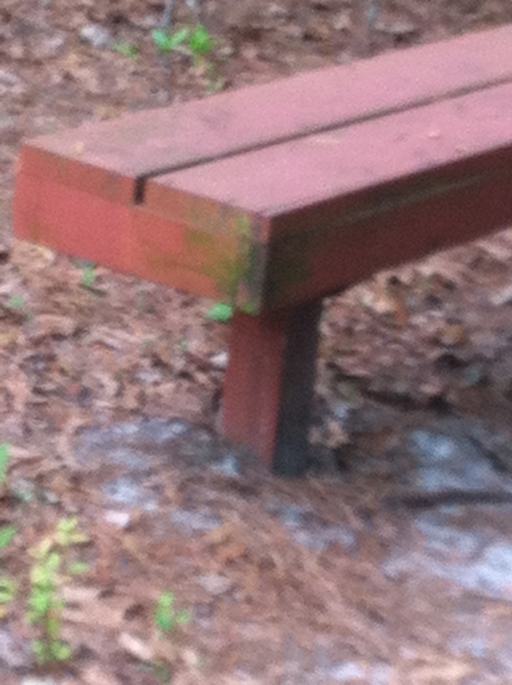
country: US
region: Georgia
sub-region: Emanuel County
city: Twin City
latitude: 32.5477
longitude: -82.1218
